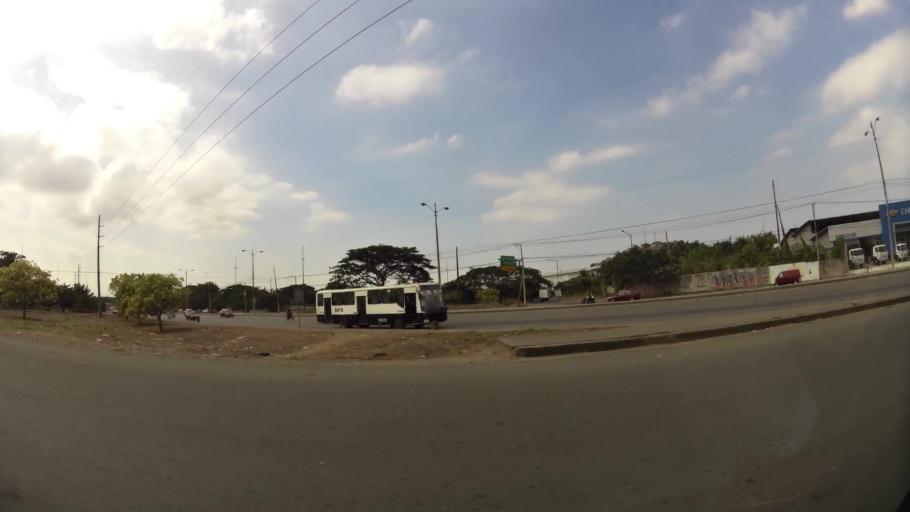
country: EC
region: Guayas
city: Santa Lucia
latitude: -2.0847
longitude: -79.9387
